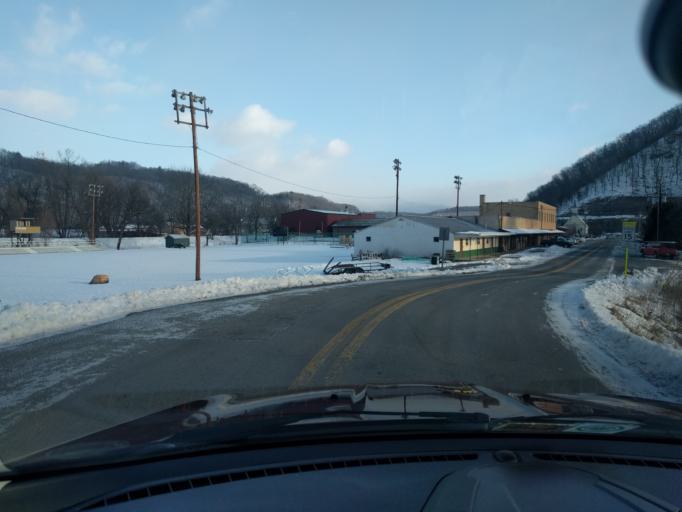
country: US
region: West Virginia
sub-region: Pocahontas County
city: Marlinton
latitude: 38.2193
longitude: -80.0946
